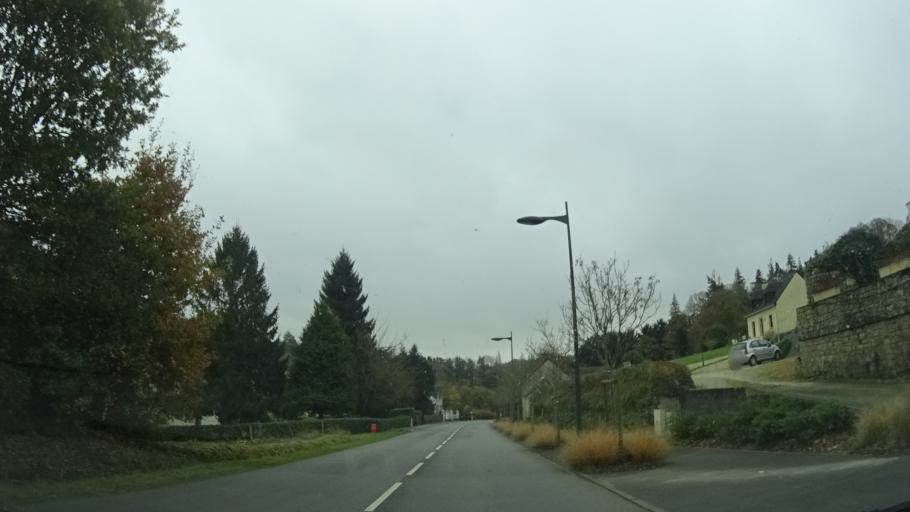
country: FR
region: Brittany
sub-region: Departement du Finistere
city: Chateaulin
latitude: 48.2193
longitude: -4.0699
